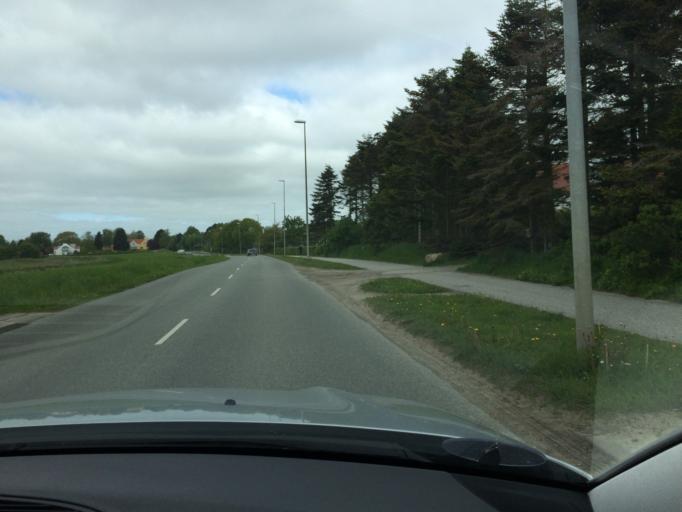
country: DK
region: Central Jutland
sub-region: Arhus Kommune
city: Hjortshoj
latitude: 56.2282
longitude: 10.3053
